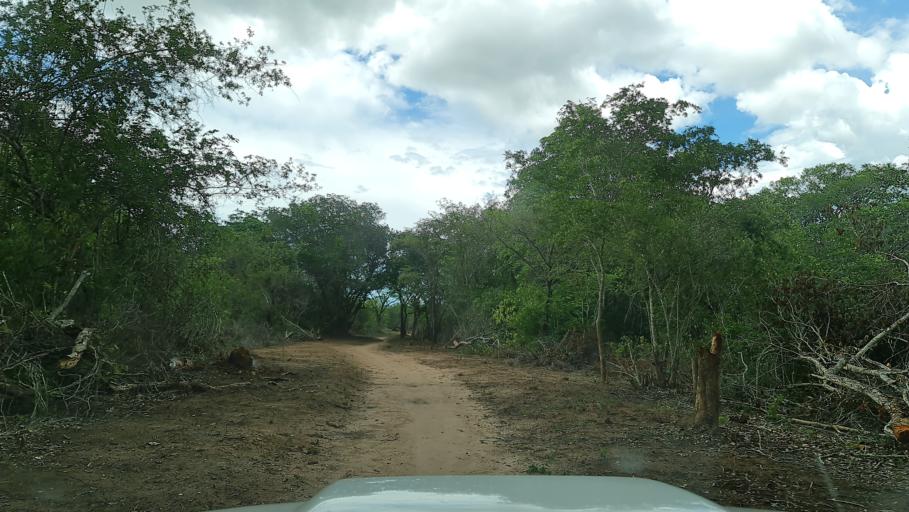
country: MZ
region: Nampula
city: Ilha de Mocambique
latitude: -15.5021
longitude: 40.1843
